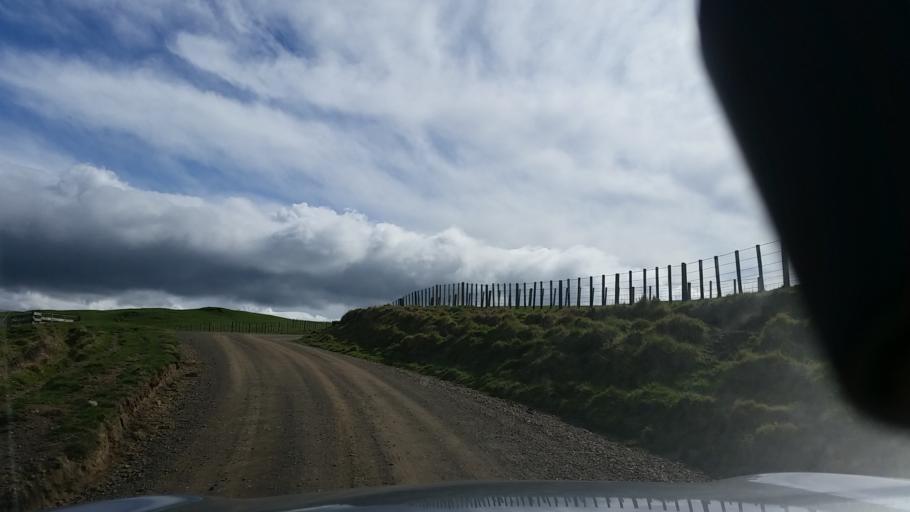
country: NZ
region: Hawke's Bay
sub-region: Napier City
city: Napier
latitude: -39.2102
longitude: 176.9588
